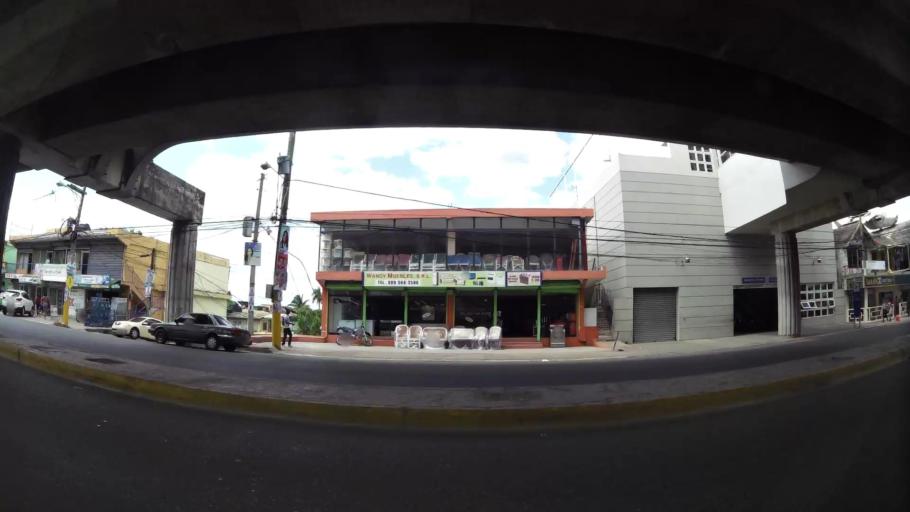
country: DO
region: Nacional
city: Ensanche Luperon
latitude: 18.5294
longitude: -69.9084
